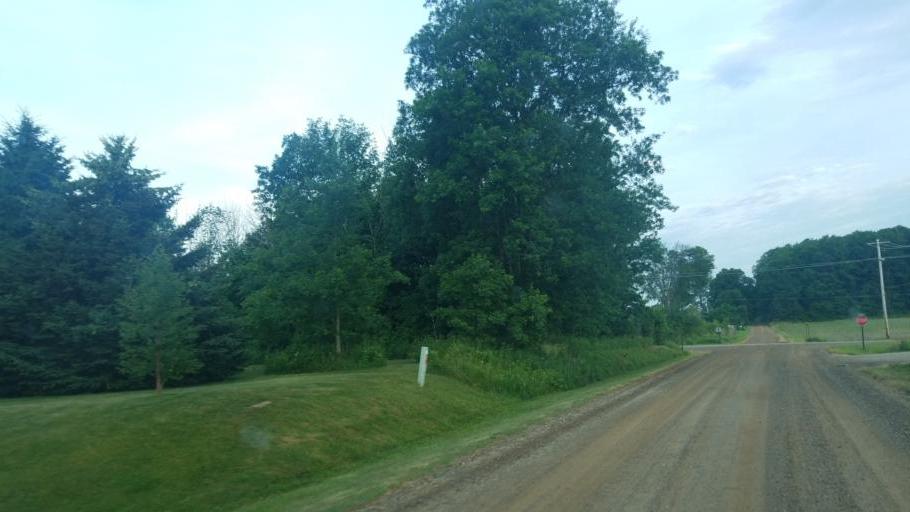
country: US
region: Michigan
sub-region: Eaton County
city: Charlotte
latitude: 42.5972
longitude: -84.9138
